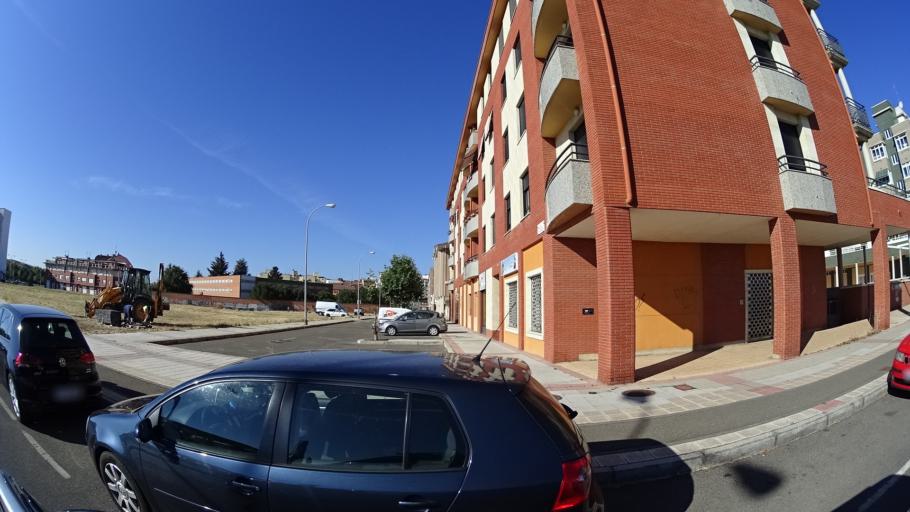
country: ES
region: Castille and Leon
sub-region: Provincia de Leon
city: Leon
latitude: 42.6022
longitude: -5.5580
